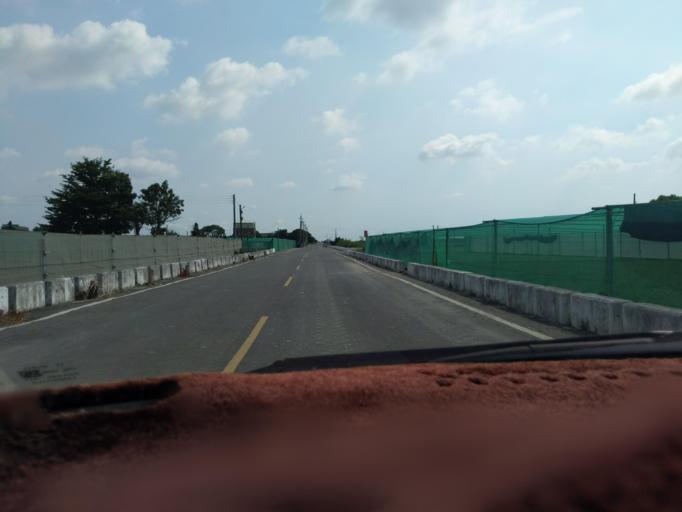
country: TW
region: Taiwan
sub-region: Yunlin
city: Douliu
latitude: 23.7888
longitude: 120.4154
